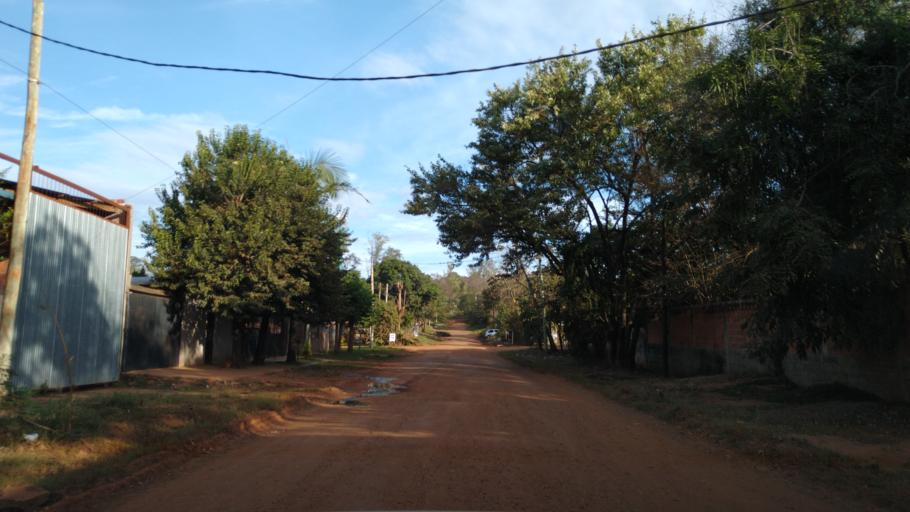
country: AR
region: Misiones
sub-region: Departamento de Capital
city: Posadas
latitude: -27.3995
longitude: -55.9258
